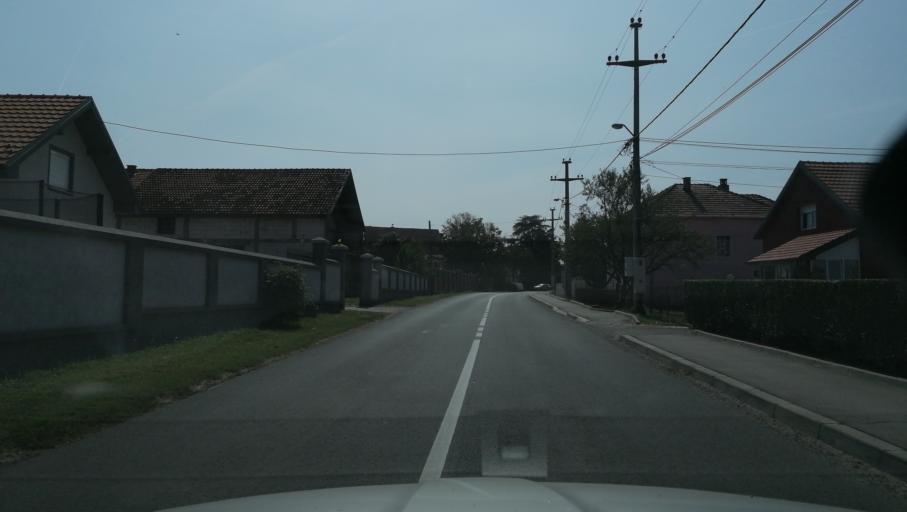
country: RS
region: Central Serbia
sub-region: Belgrade
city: Zvezdara
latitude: 44.6921
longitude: 20.5530
